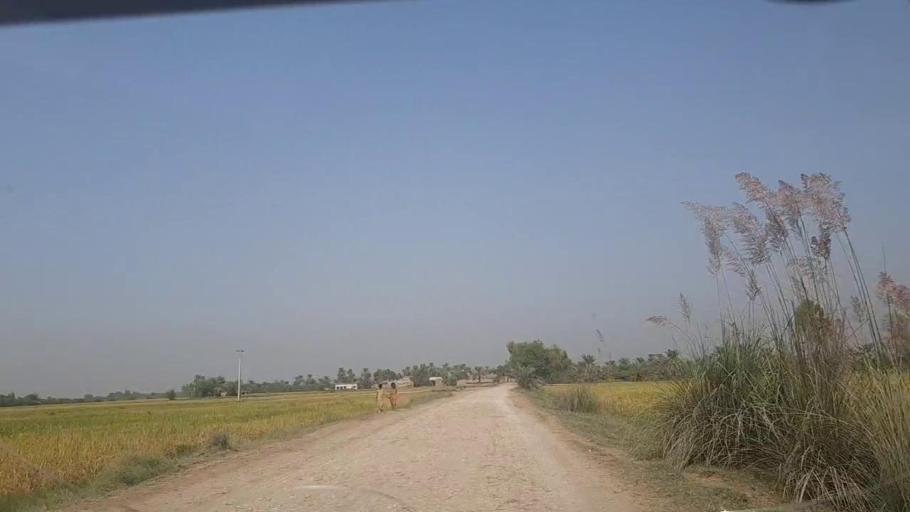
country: PK
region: Sindh
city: Madeji
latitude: 27.8038
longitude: 68.4260
